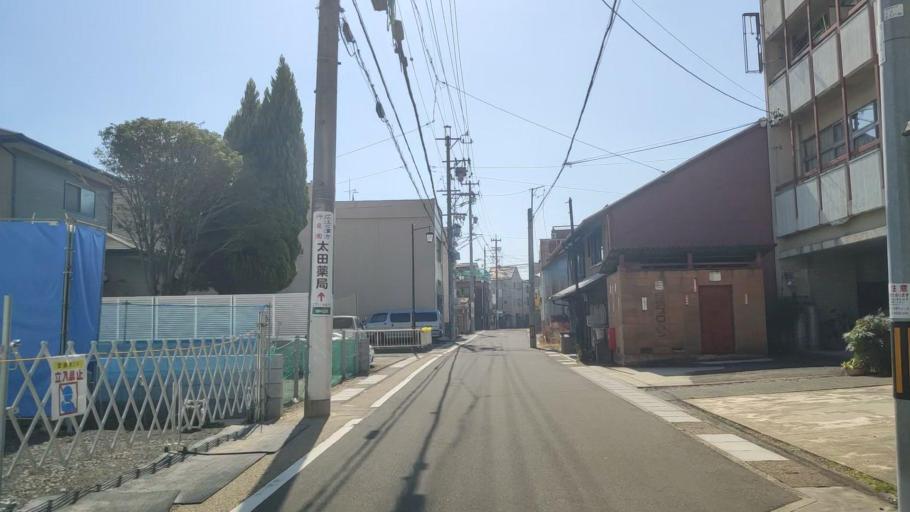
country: JP
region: Gifu
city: Gifu-shi
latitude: 35.4068
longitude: 136.7627
